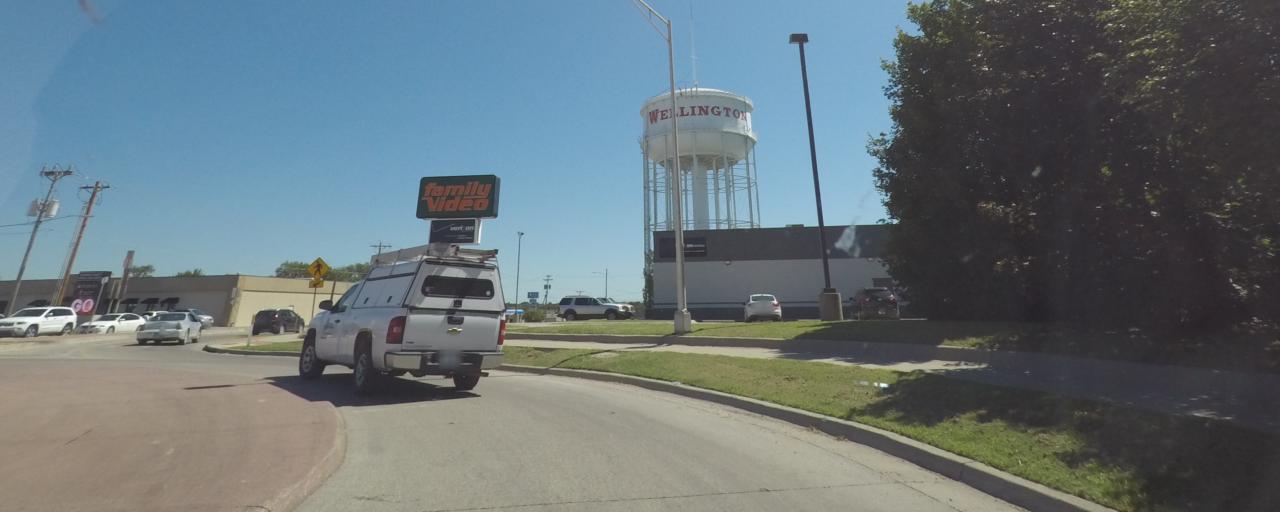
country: US
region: Kansas
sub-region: Sumner County
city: Wellington
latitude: 37.2747
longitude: -97.3940
